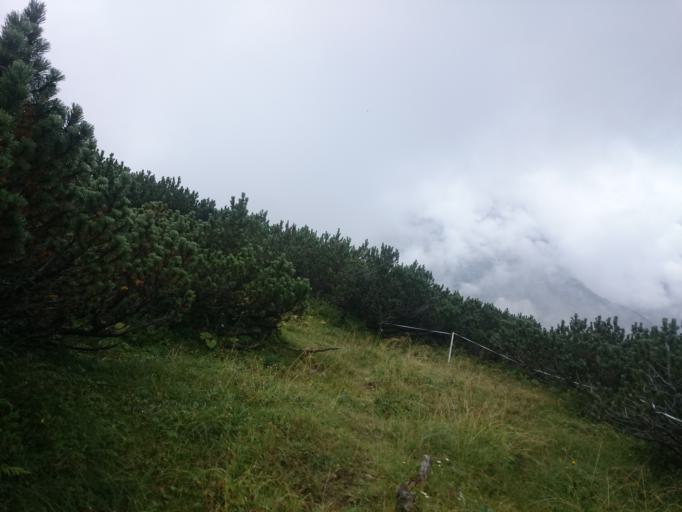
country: AT
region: Tyrol
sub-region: Politischer Bezirk Innsbruck Land
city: Absam
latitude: 47.4027
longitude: 11.5024
